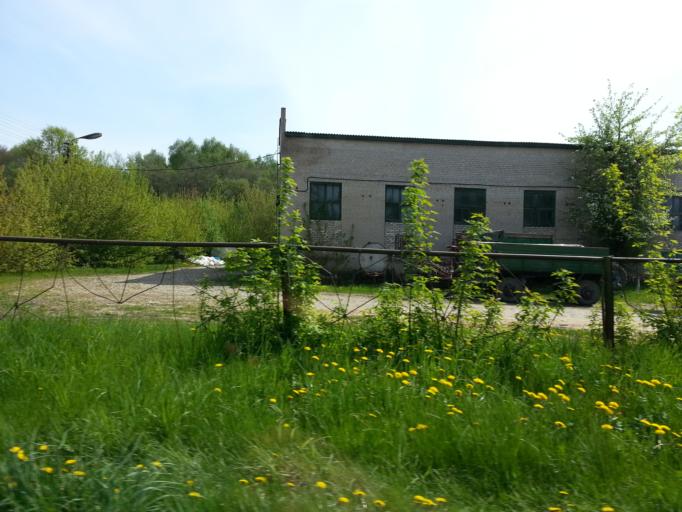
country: LT
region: Panevezys
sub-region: Panevezys City
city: Panevezys
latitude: 55.8991
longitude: 24.2376
